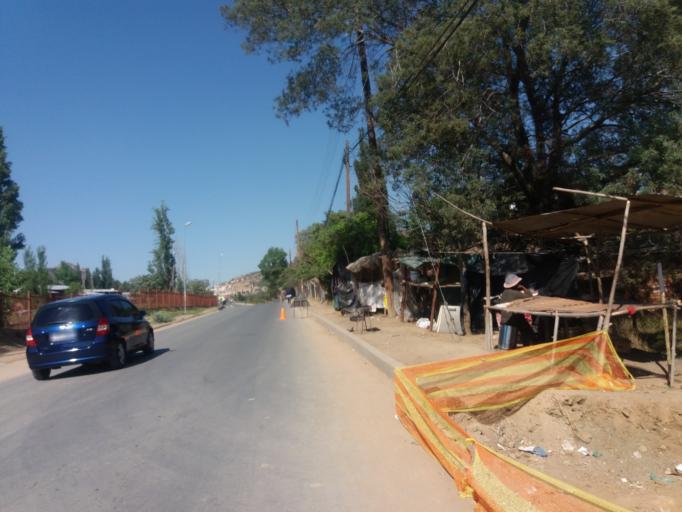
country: LS
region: Maseru
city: Maseru
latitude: -29.3205
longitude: 27.5051
